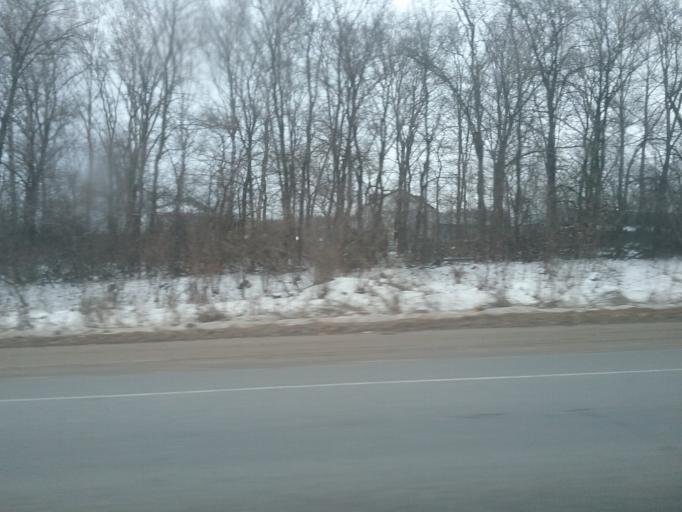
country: RU
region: Tula
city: Skuratovskiy
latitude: 54.1281
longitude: 37.6819
